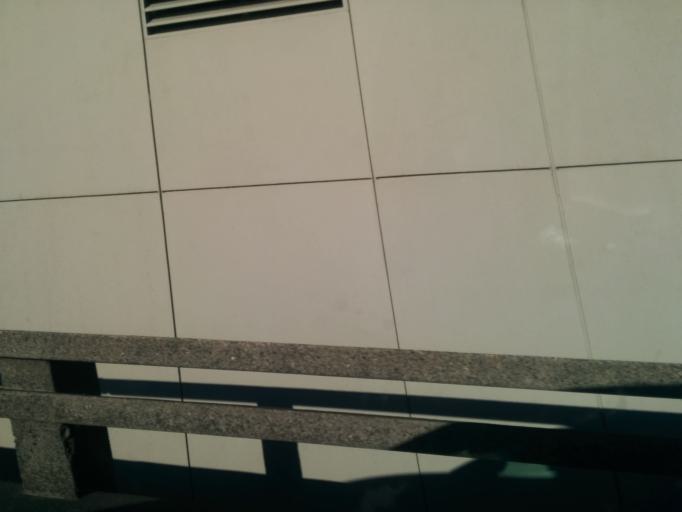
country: US
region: Washington
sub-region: King County
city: Seattle
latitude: 47.6111
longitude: -122.3458
